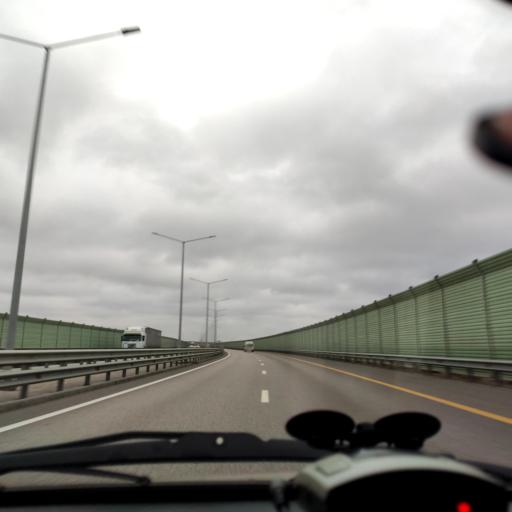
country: RU
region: Voronezj
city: Novaya Usman'
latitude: 51.6054
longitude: 39.3279
